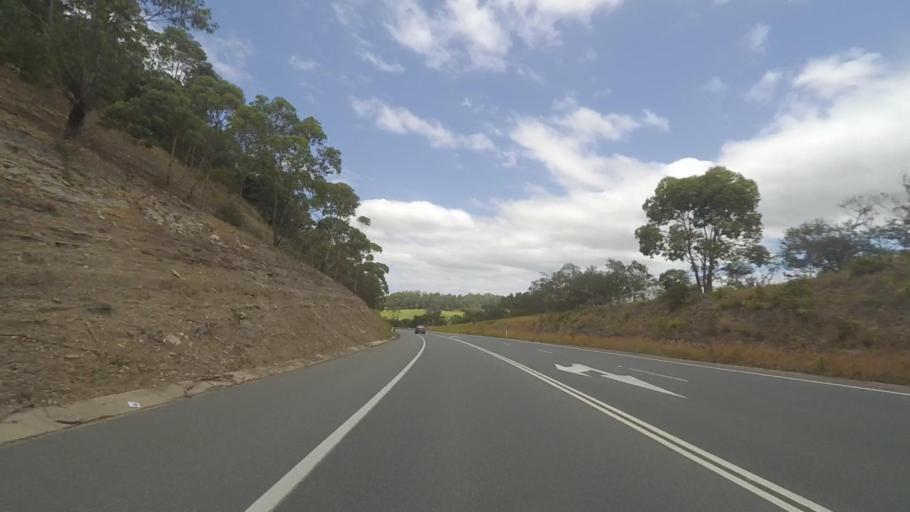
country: AU
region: New South Wales
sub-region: Shoalhaven Shire
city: Milton
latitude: -35.2643
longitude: 150.4257
